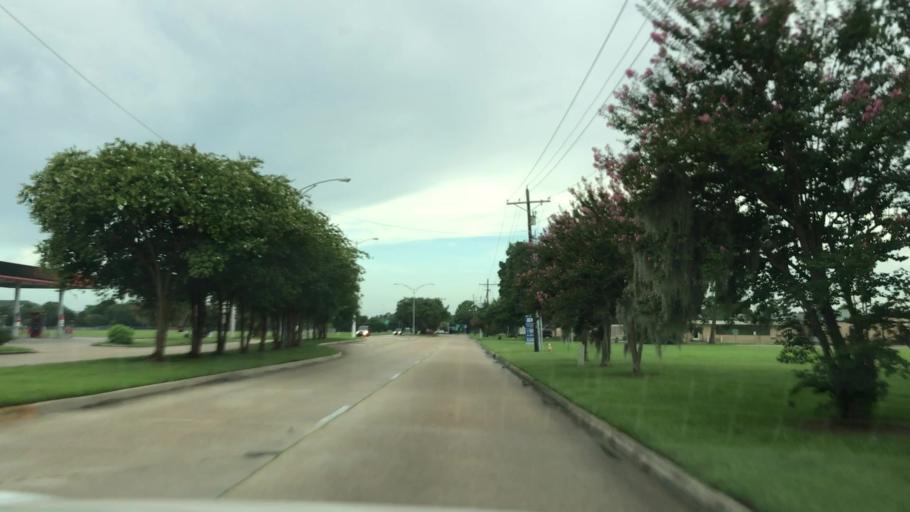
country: US
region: Louisiana
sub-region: East Baton Rouge Parish
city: Brownsfield
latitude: 30.5264
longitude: -91.1612
